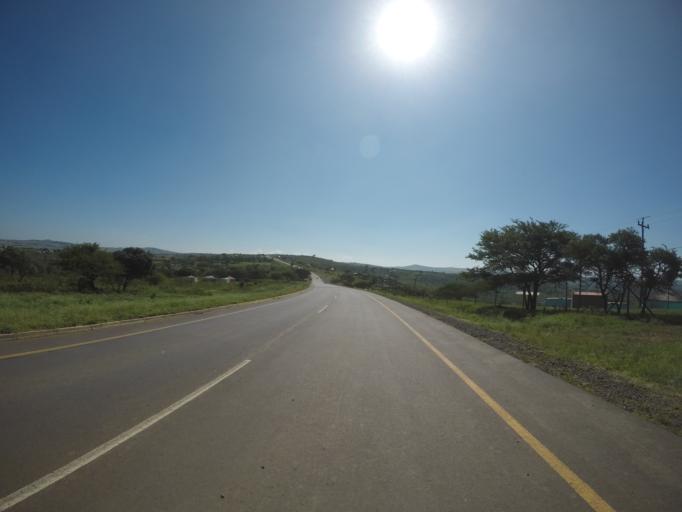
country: ZA
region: KwaZulu-Natal
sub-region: uThungulu District Municipality
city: Empangeni
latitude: -28.5624
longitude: 31.7062
